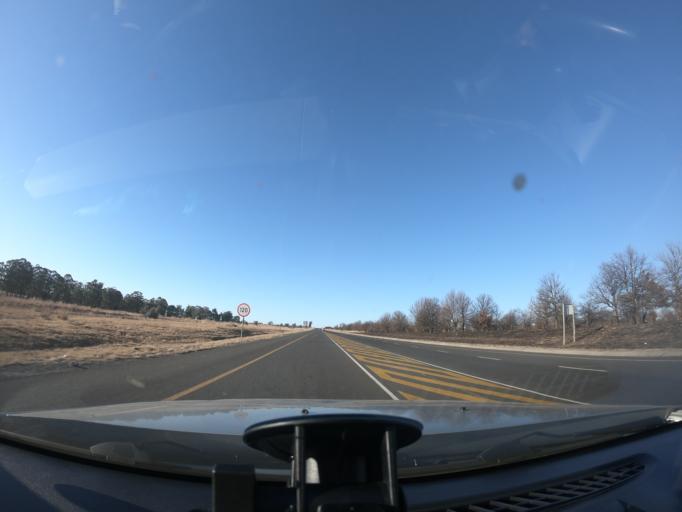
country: ZA
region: Mpumalanga
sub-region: Gert Sibande District Municipality
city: Ermelo
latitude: -26.4667
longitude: 29.9548
